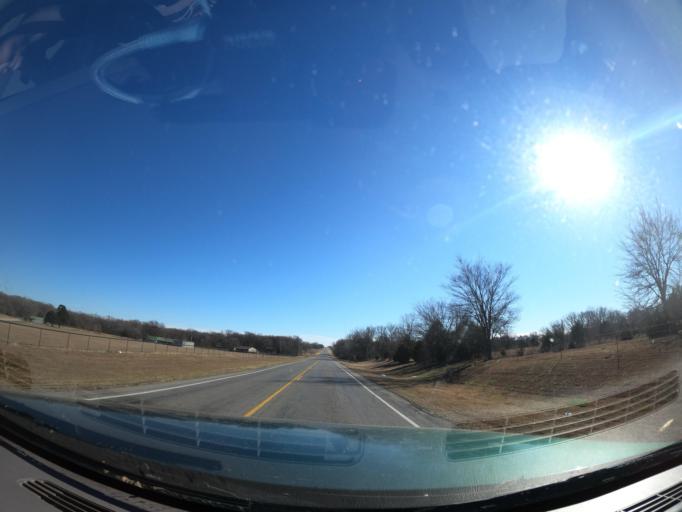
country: US
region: Oklahoma
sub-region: Muskogee County
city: Haskell
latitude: 35.7751
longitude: -95.6572
